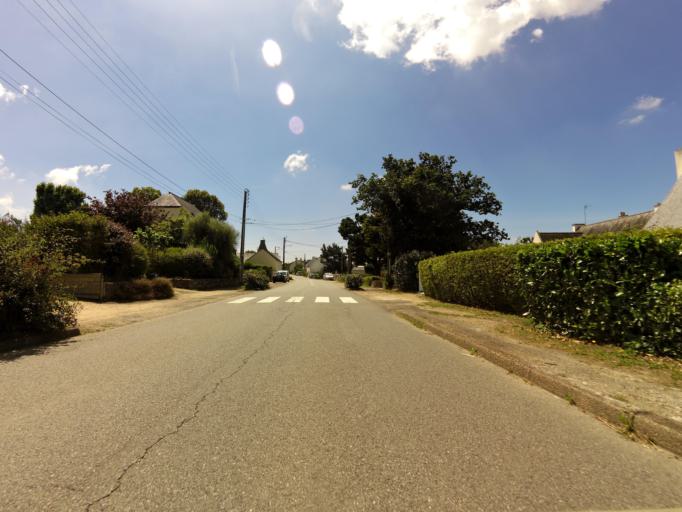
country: FR
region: Brittany
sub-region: Departement du Morbihan
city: Theix
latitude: 47.6127
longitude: -2.6834
